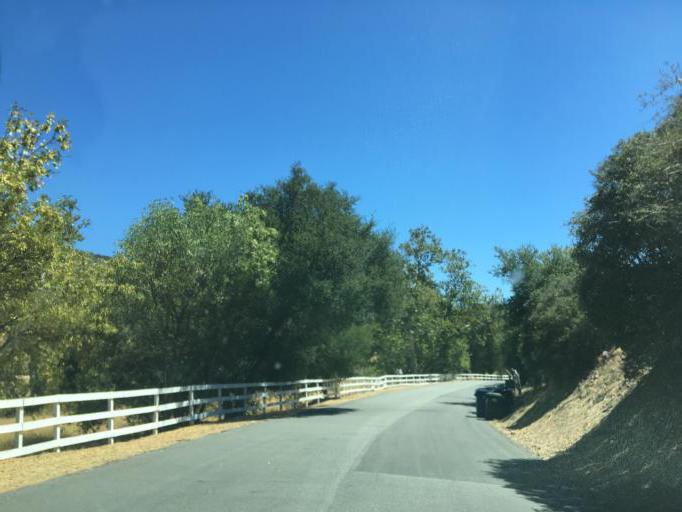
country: US
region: California
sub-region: Los Angeles County
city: Westlake Village
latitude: 34.1188
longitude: -118.8105
